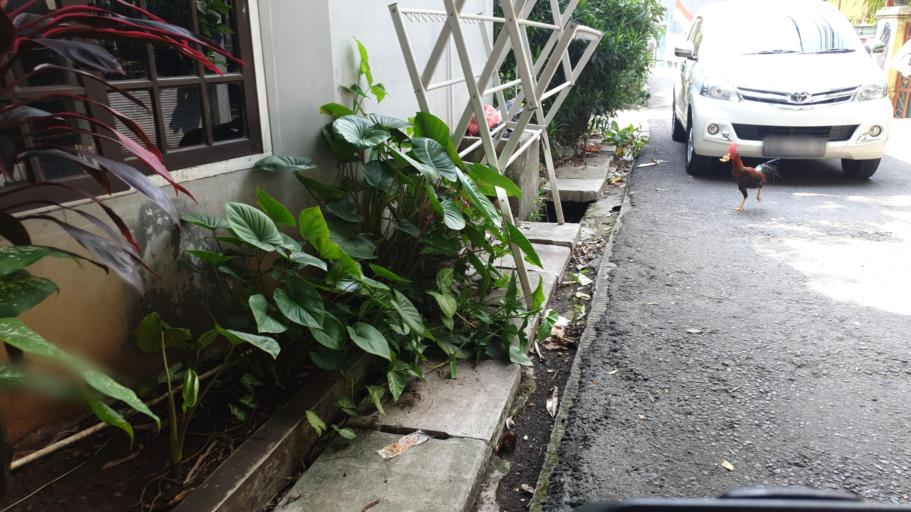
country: ID
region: West Java
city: Depok
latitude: -6.3627
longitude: 106.8357
